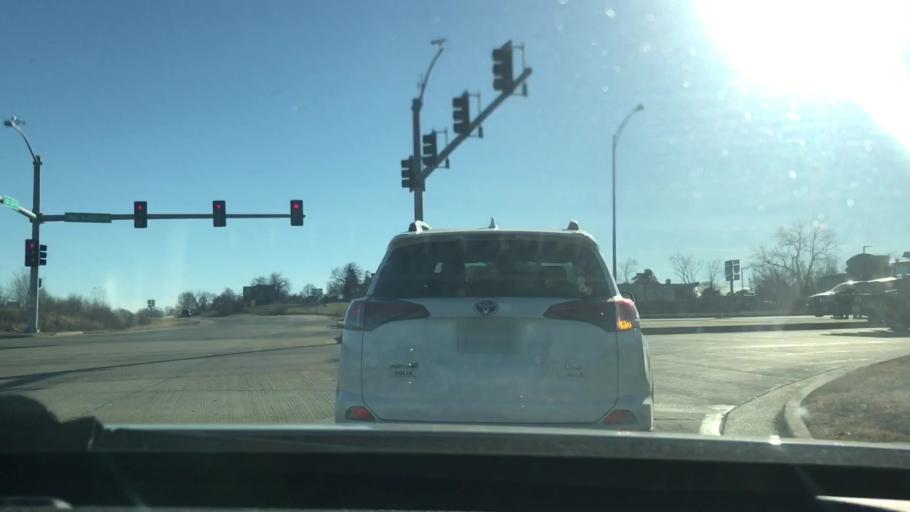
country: US
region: Missouri
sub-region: Jackson County
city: Grandview
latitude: 38.9240
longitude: -94.5292
